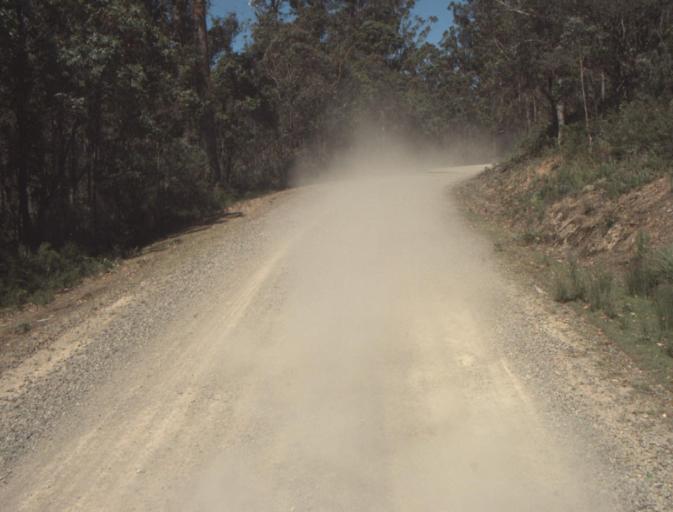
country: AU
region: Tasmania
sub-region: Dorset
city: Scottsdale
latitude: -41.3894
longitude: 147.5079
